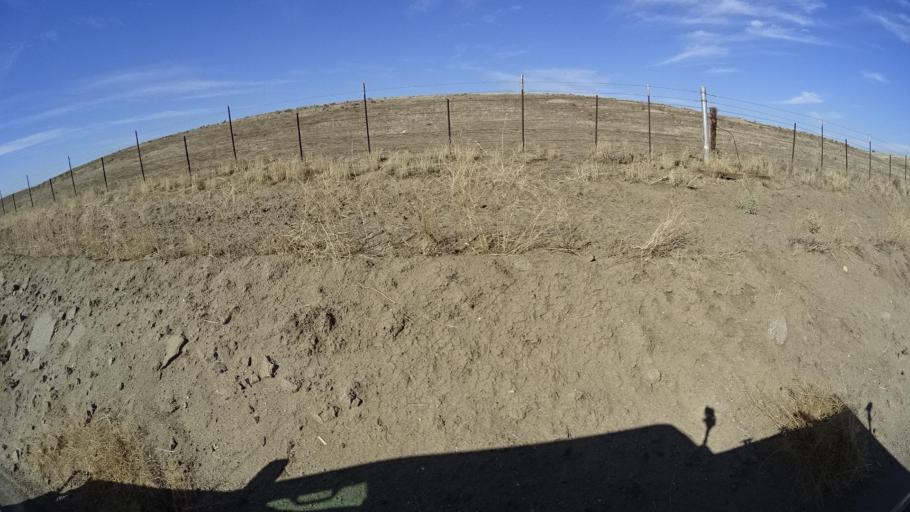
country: US
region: California
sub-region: Kern County
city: Oildale
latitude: 35.6291
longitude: -118.9736
